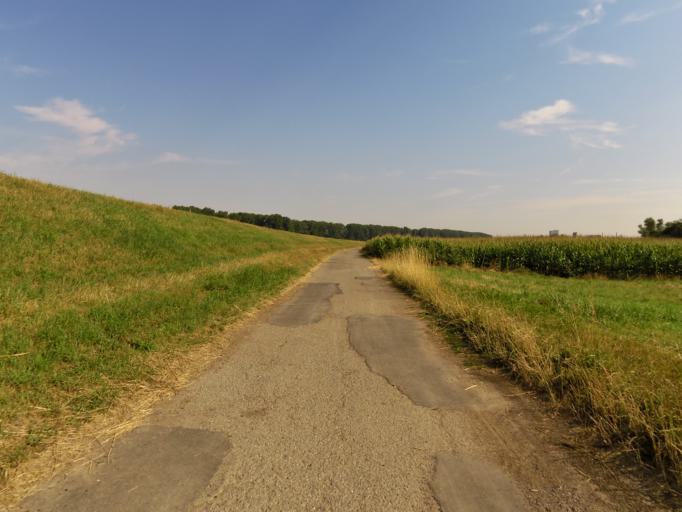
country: DE
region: Hesse
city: Lampertheim
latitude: 49.5568
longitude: 8.4208
